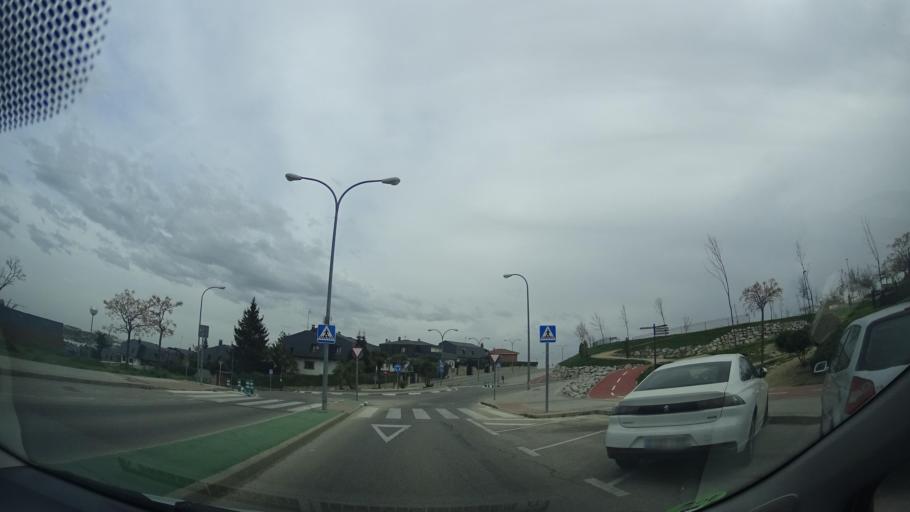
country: ES
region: Madrid
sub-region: Provincia de Madrid
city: Colmenar Viejo
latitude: 40.6657
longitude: -3.7652
